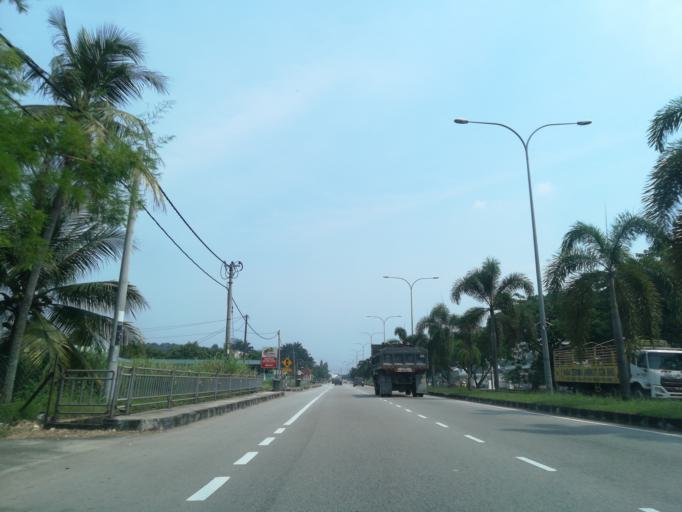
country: MY
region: Kedah
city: Kulim
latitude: 5.4026
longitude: 100.5548
